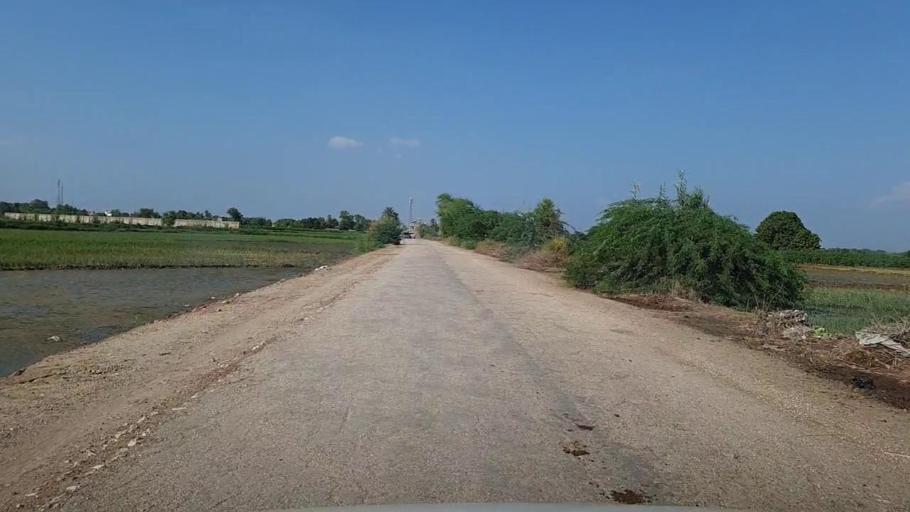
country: PK
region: Sindh
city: Kandiaro
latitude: 27.0762
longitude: 68.3127
